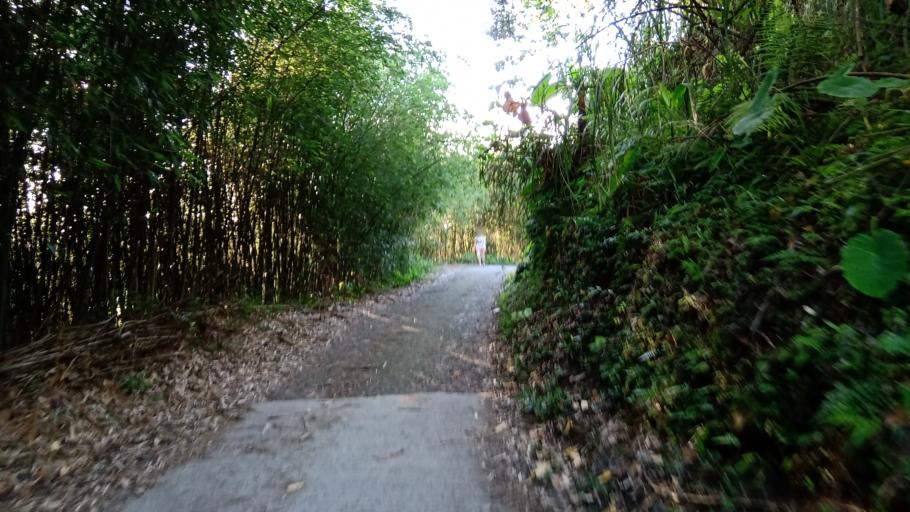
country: TW
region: Taiwan
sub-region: Miaoli
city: Miaoli
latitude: 24.4195
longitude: 120.9218
